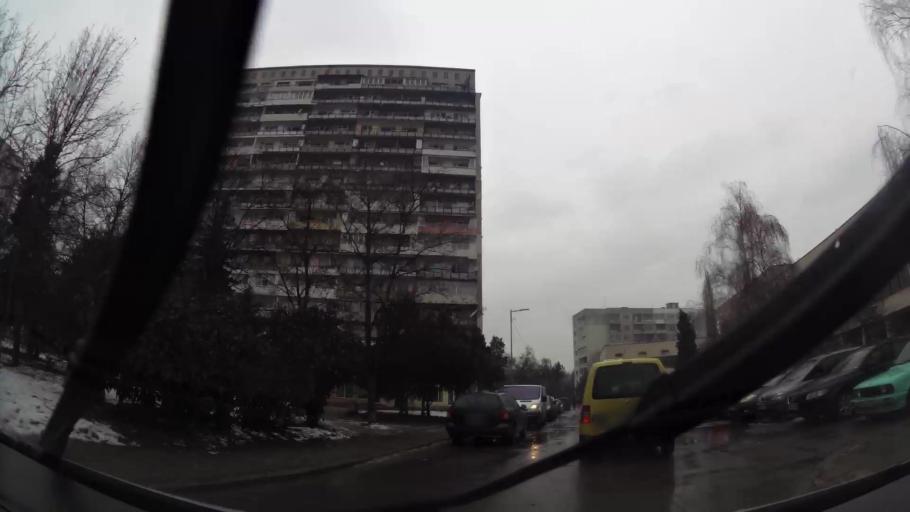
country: BG
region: Sofia-Capital
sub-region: Stolichna Obshtina
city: Sofia
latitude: 42.6641
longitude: 23.2971
